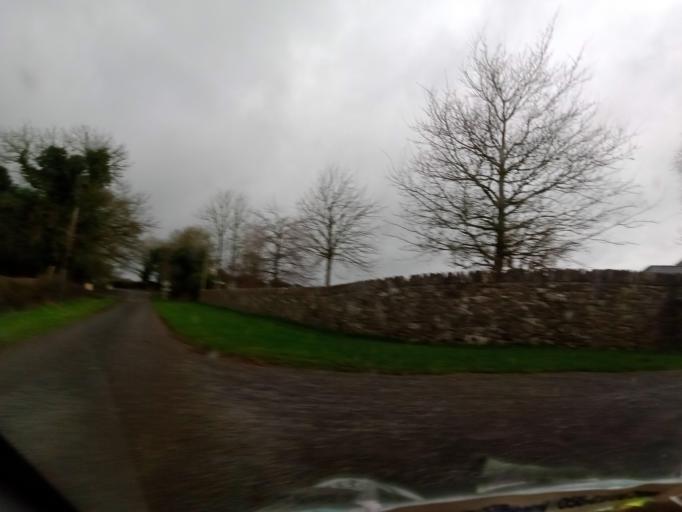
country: IE
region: Munster
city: Cashel
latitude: 52.5435
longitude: -7.8247
